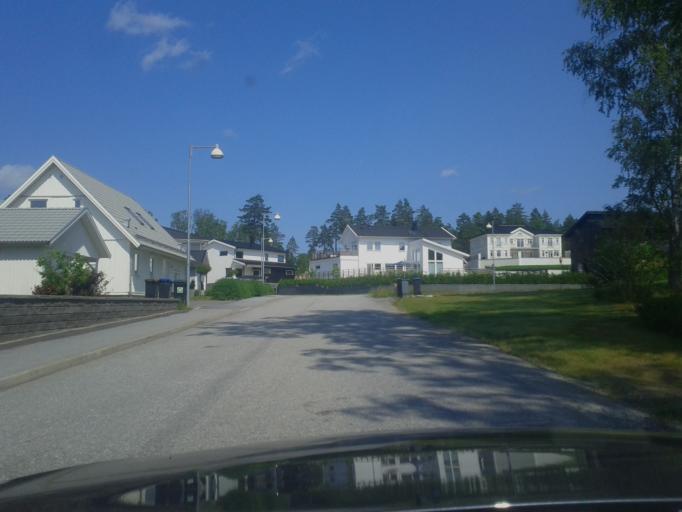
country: SE
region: Stockholm
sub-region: Vallentuna Kommun
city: Vallentuna
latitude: 59.5022
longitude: 18.0927
